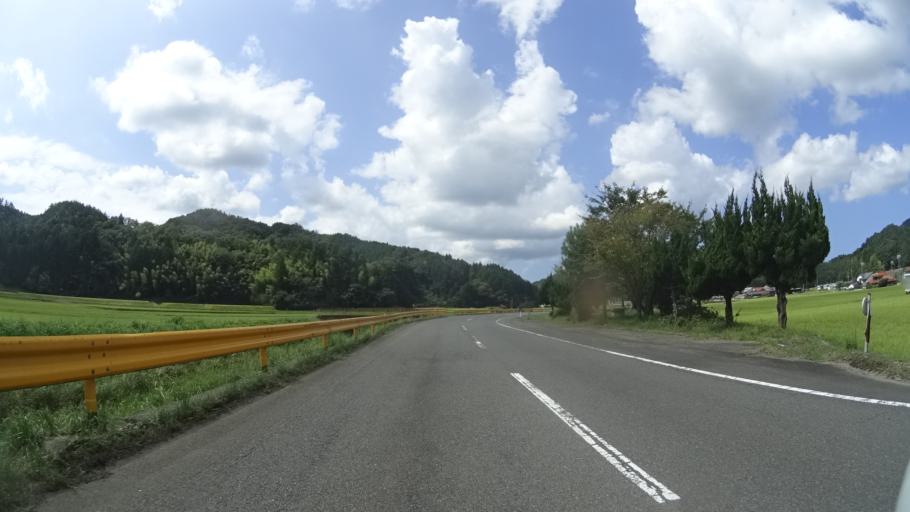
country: JP
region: Yamaguchi
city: Hagi
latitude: 34.5150
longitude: 131.6029
